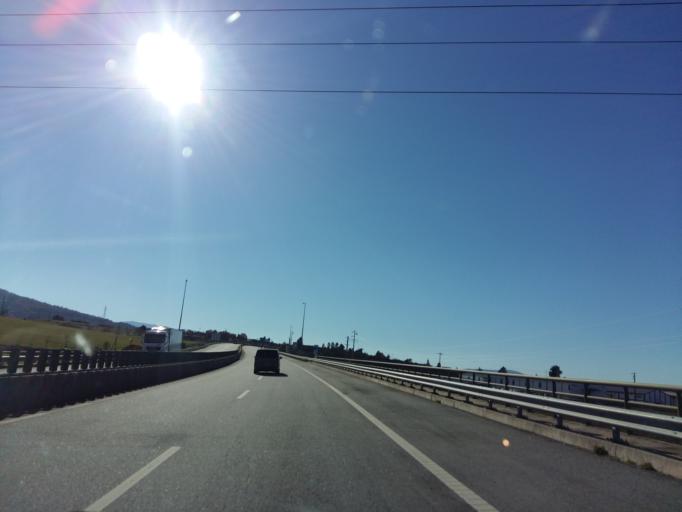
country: PT
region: Castelo Branco
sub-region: Covilha
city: Covilha
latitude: 40.2377
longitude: -7.4825
